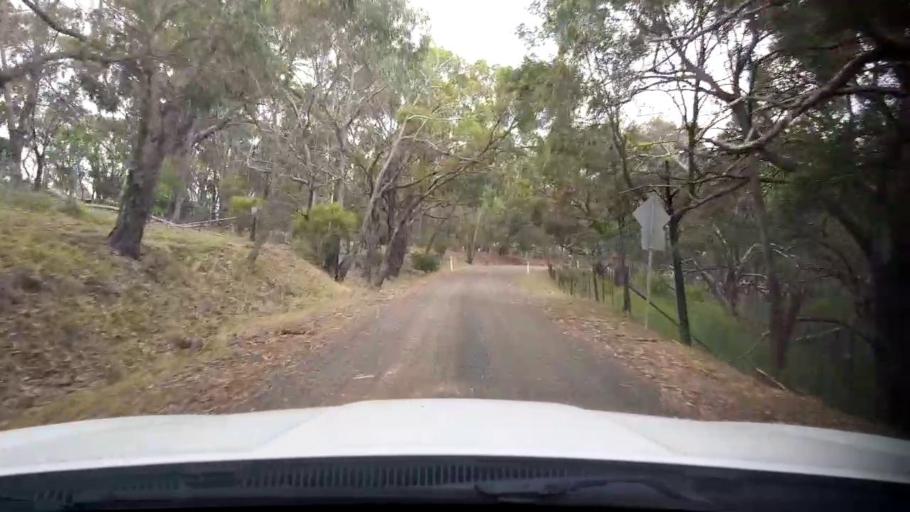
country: AU
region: Victoria
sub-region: Whittlesea
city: Whittlesea
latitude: -37.4834
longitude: 145.0505
